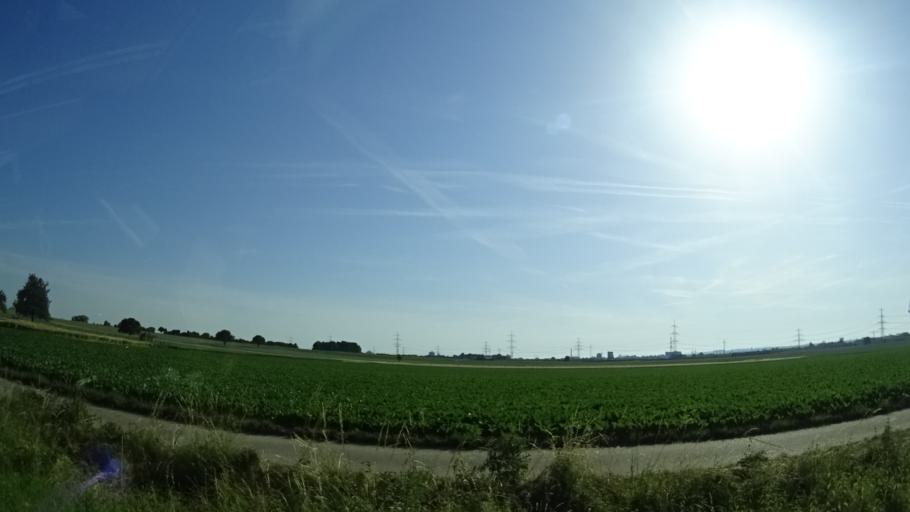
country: DE
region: Hesse
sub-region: Regierungsbezirk Darmstadt
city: Eschborn
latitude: 50.1442
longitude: 8.5811
